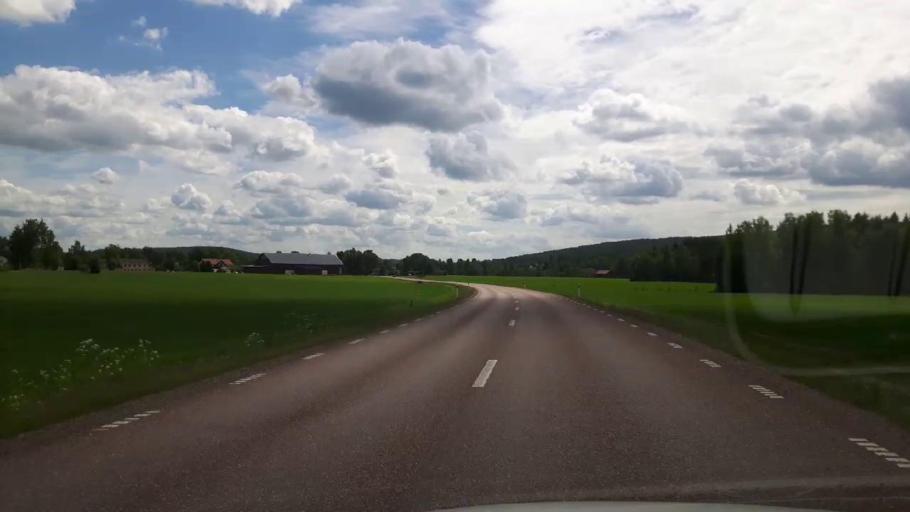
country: SE
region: Dalarna
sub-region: Saters Kommun
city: Saeter
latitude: 60.4014
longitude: 15.8750
